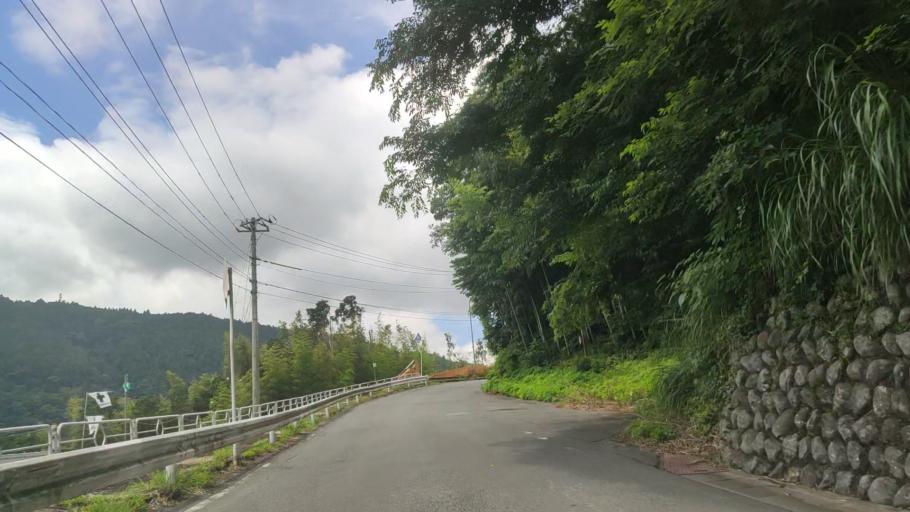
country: JP
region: Shizuoka
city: Fujinomiya
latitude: 35.2421
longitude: 138.4972
